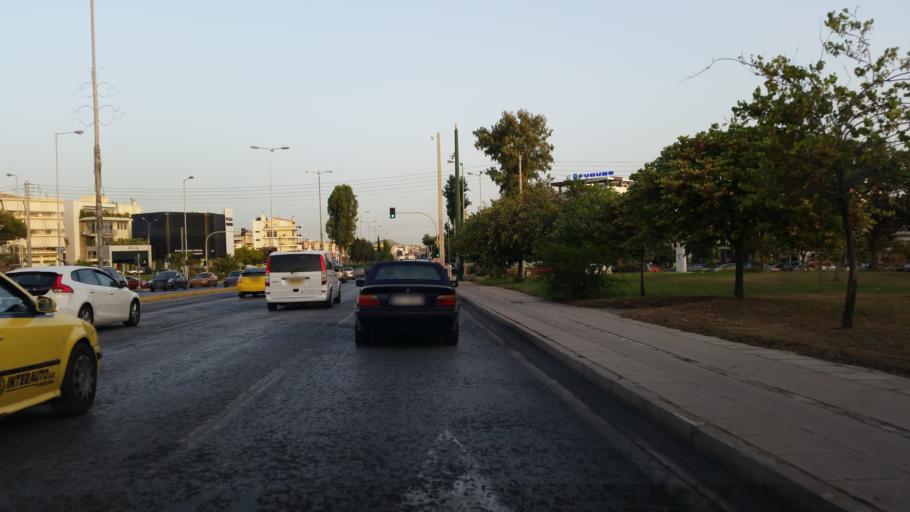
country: GR
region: Attica
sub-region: Nomarchia Athinas
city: Glyfada
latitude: 37.8763
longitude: 23.7560
